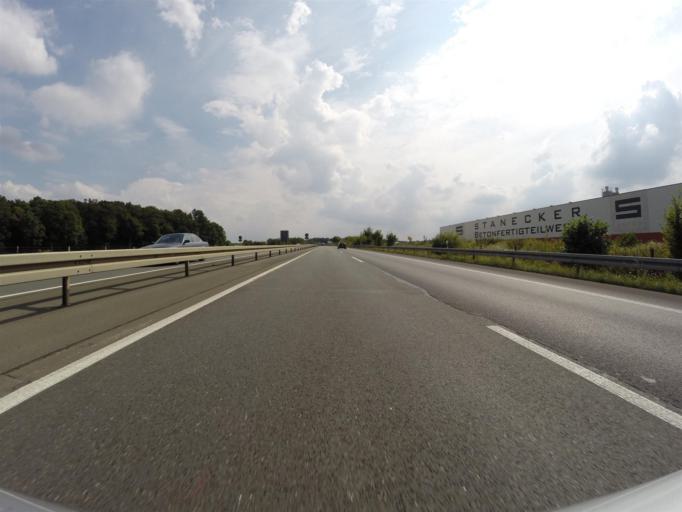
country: DE
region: North Rhine-Westphalia
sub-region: Regierungsbezirk Detmold
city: Paderborn
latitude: 51.6247
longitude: 8.7263
